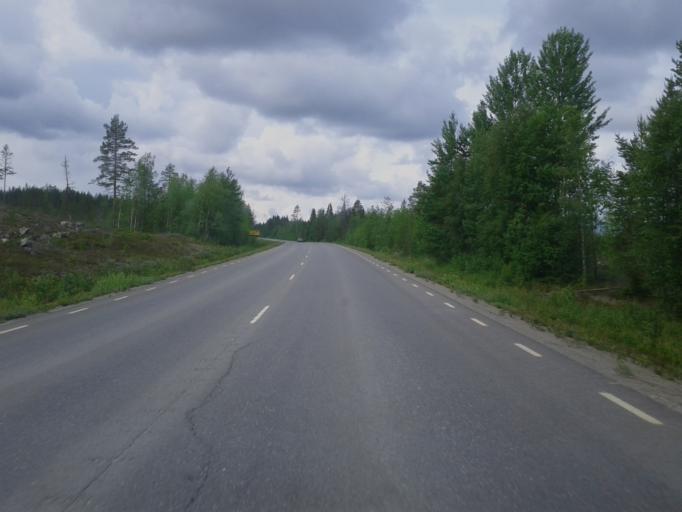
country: SE
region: Vaesterbotten
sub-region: Norsjo Kommun
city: Norsjoe
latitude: 64.9869
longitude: 19.4654
